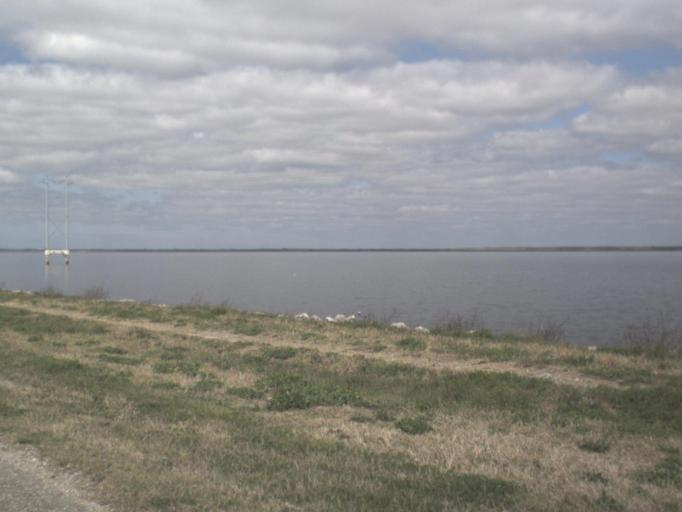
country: US
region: Florida
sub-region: Franklin County
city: Eastpoint
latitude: 29.7347
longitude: -84.9068
